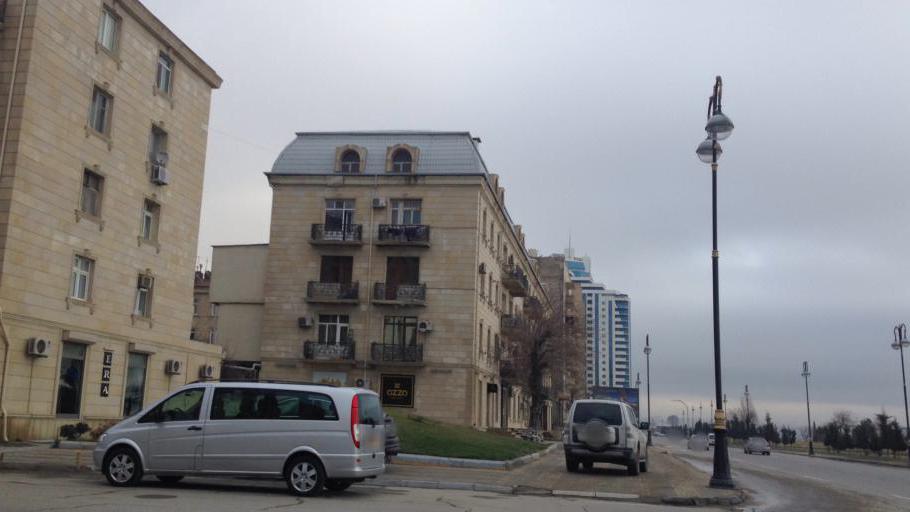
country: AZ
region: Baki
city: Baku
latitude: 40.3771
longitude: 49.8685
